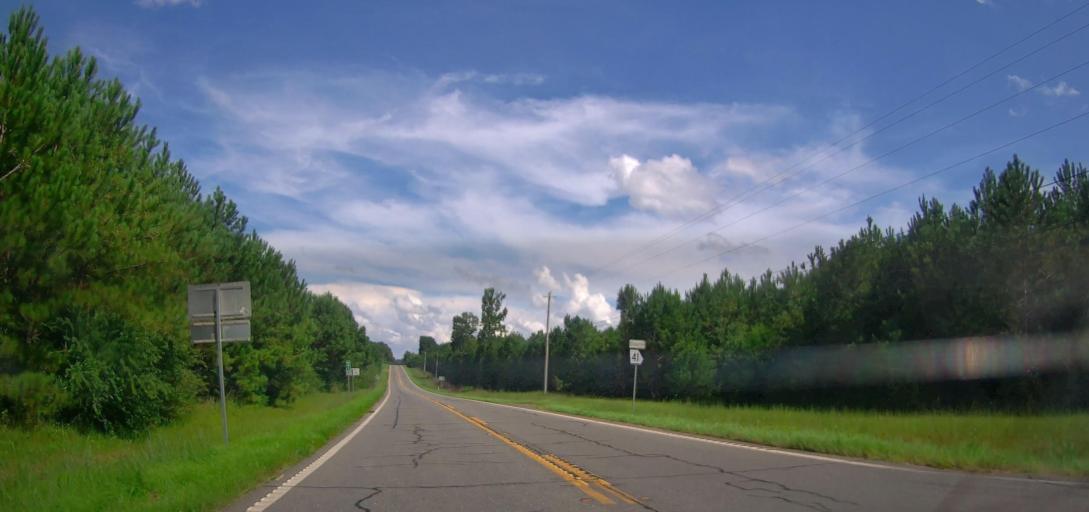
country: US
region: Georgia
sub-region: Talbot County
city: Sardis
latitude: 32.8004
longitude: -84.5870
